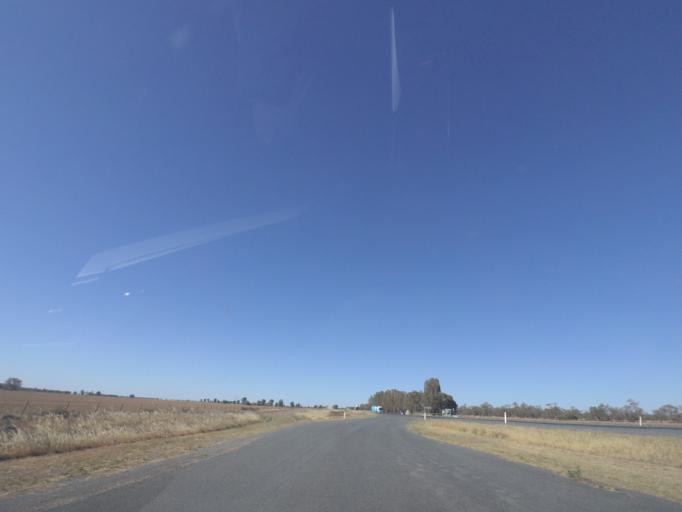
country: AU
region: New South Wales
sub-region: Bland
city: West Wyalong
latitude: -33.7652
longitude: 147.5184
